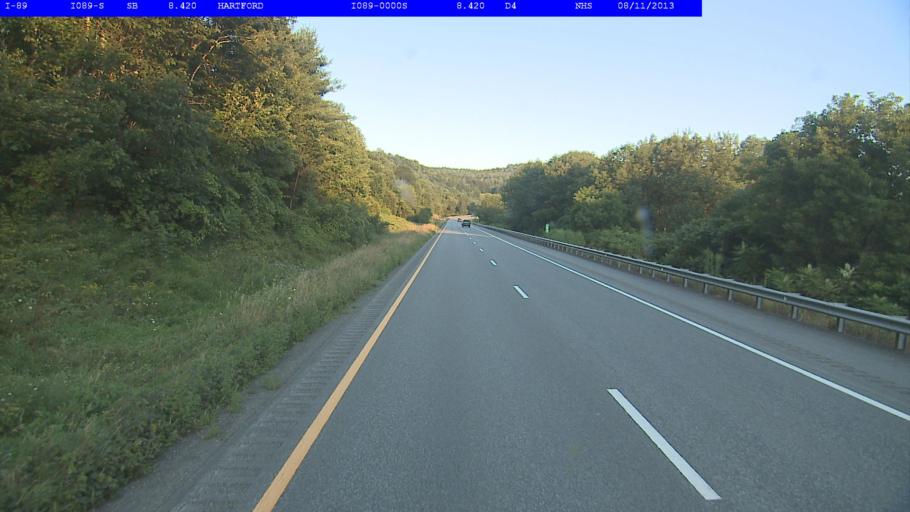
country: US
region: Vermont
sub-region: Windsor County
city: Wilder
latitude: 43.7236
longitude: -72.4208
